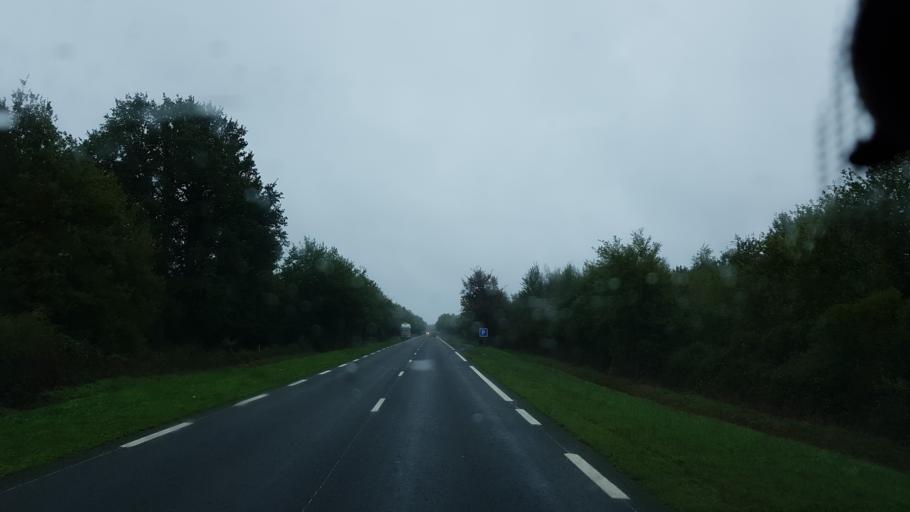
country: FR
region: Centre
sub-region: Departement du Loir-et-Cher
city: Salbris
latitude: 47.4670
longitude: 2.0413
